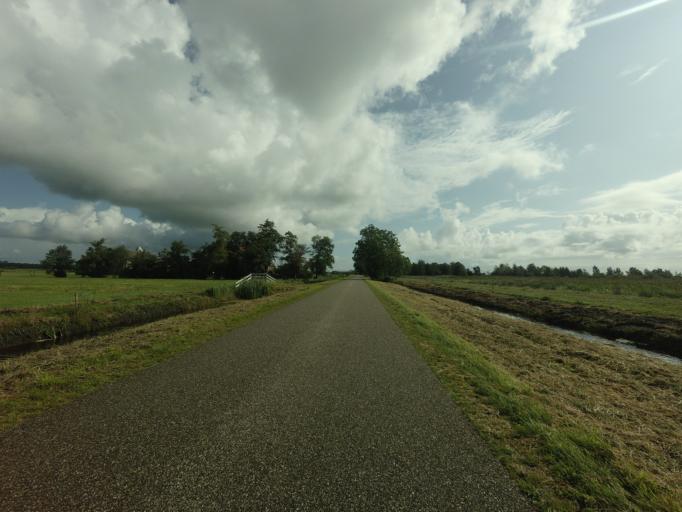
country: NL
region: Friesland
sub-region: Gemeente Boarnsterhim
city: Warten
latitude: 53.1475
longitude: 5.9298
